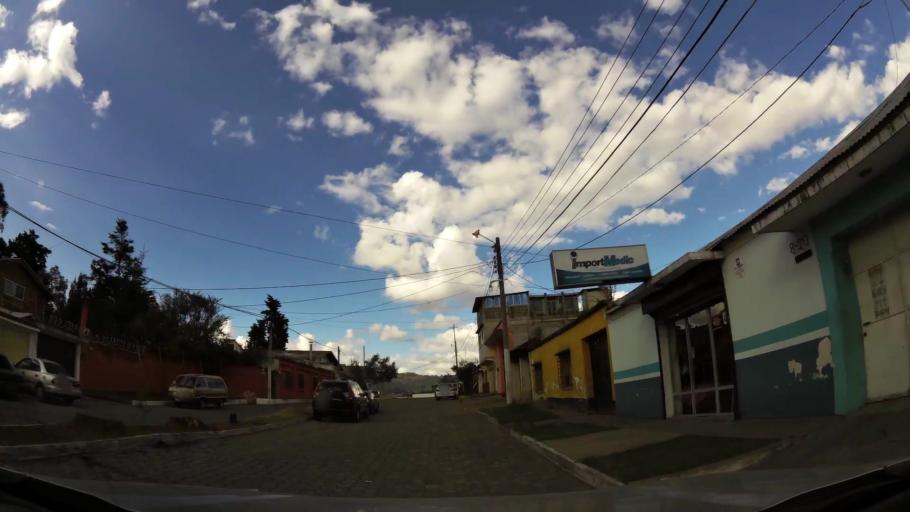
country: GT
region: Quetzaltenango
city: Quetzaltenango
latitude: 14.8479
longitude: -91.5157
